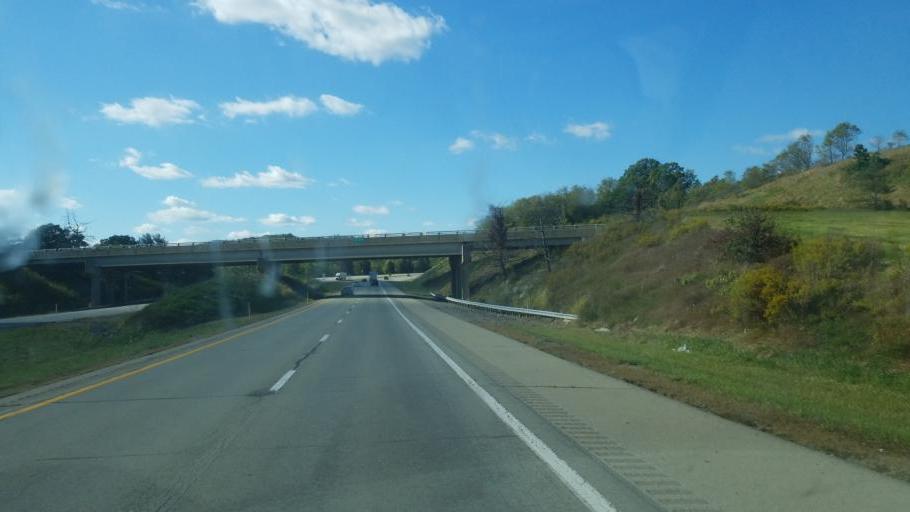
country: US
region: Pennsylvania
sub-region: Greene County
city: Morrisville
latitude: 39.8061
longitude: -80.0895
